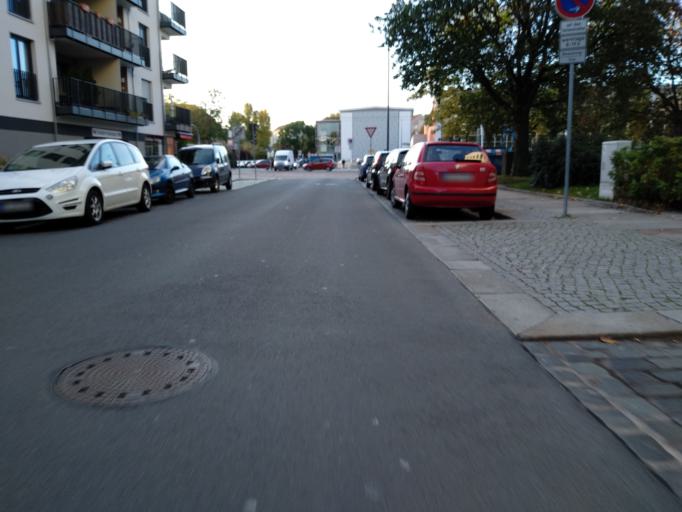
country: DE
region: Saxony
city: Dresden
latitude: 51.0508
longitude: 13.7247
